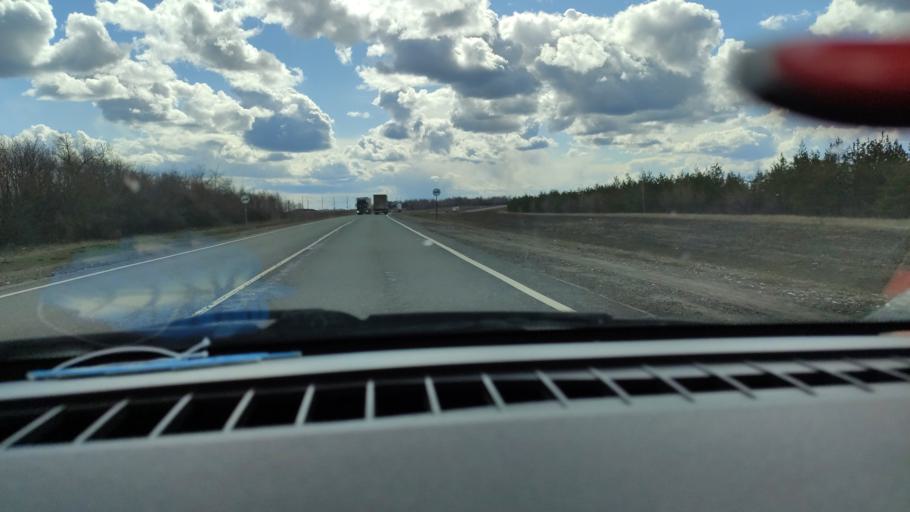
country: RU
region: Samara
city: Syzran'
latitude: 52.8677
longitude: 48.2786
